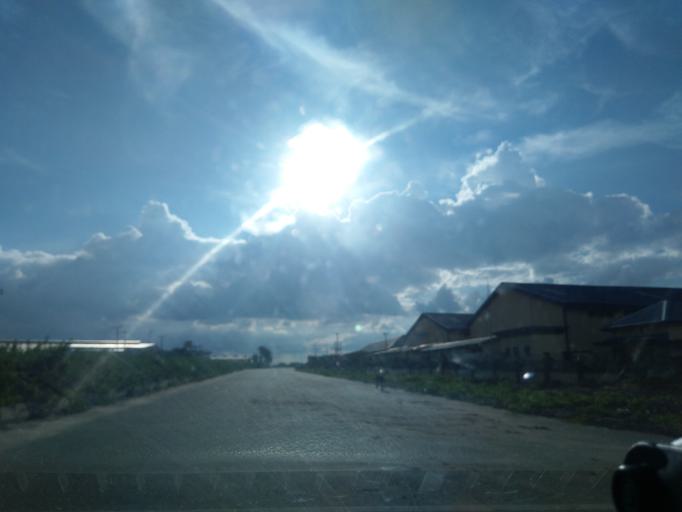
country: NG
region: Abuja Federal Capital Territory
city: Abuja
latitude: 9.0298
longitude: 7.4023
